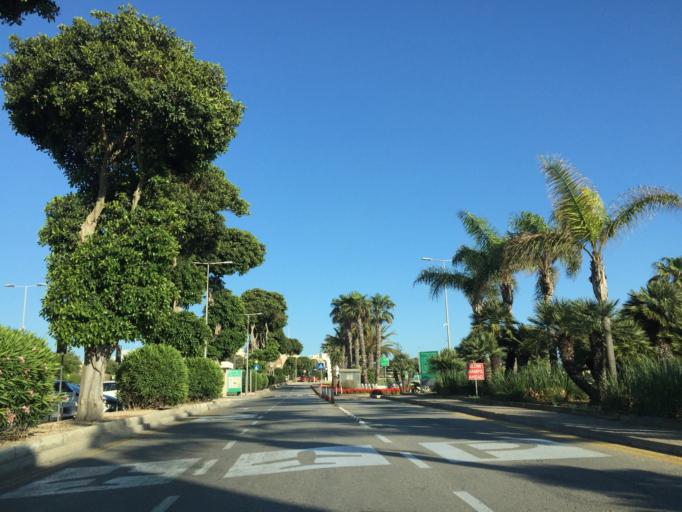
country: MT
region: Il-Gudja
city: Gudja
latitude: 35.8499
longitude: 14.4971
